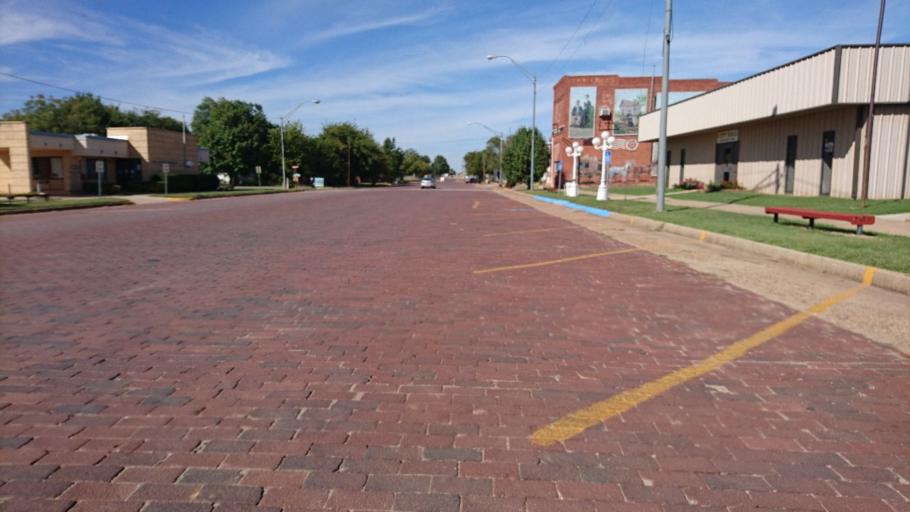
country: US
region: Oklahoma
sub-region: Lincoln County
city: Stroud
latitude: 35.7052
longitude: -96.7651
